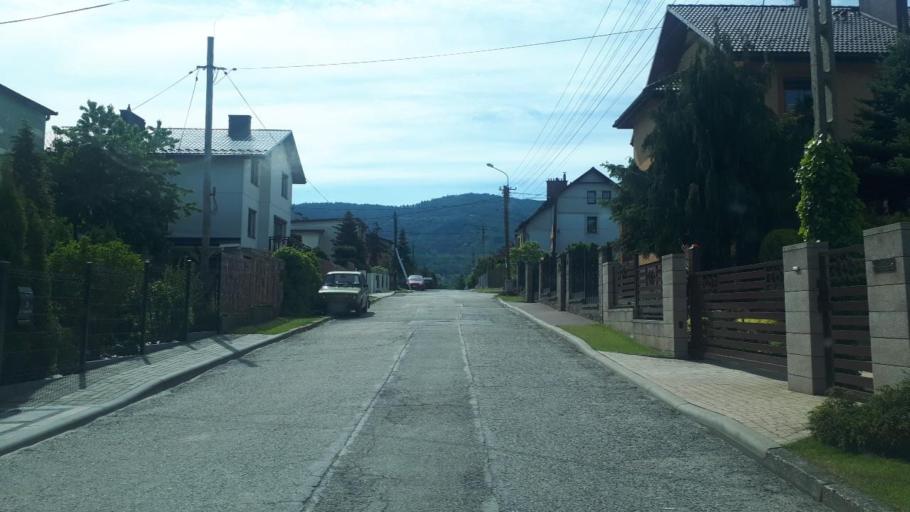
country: PL
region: Silesian Voivodeship
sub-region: Powiat bielski
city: Kozy
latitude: 49.8457
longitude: 19.1483
